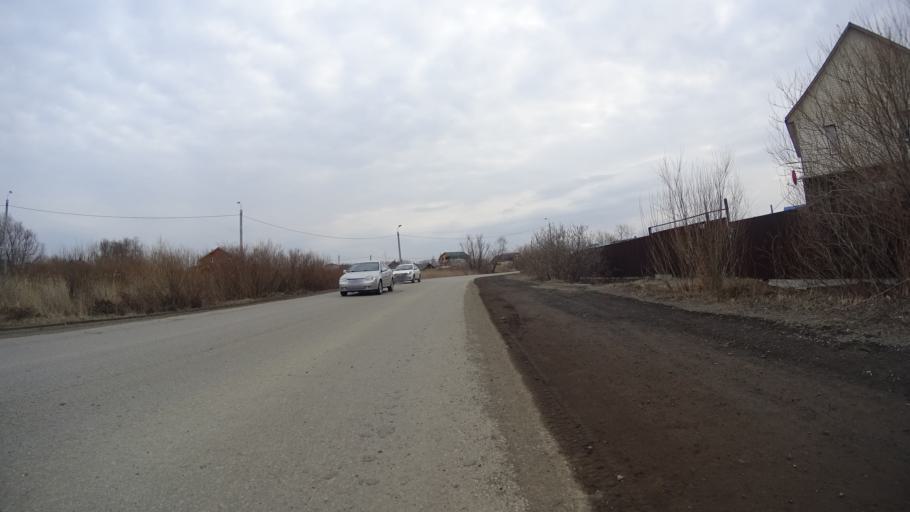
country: RU
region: Chelyabinsk
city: Zheleznodorozhnyy
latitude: 55.1673
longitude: 61.5394
